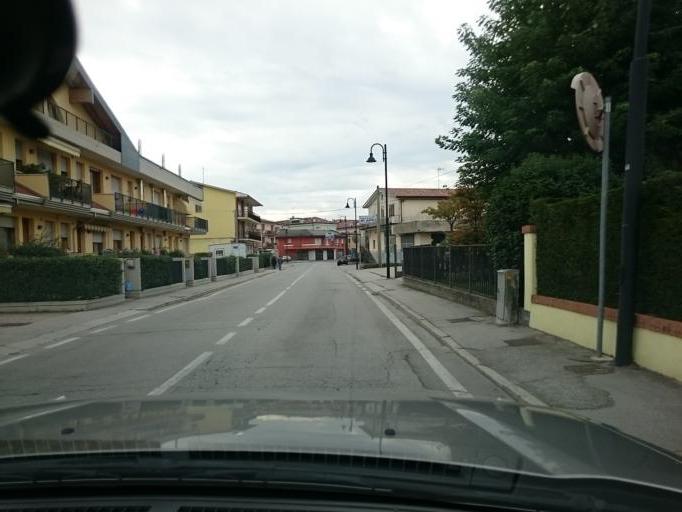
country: IT
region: Veneto
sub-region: Provincia di Padova
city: Legnaro
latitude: 45.3470
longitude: 11.9634
